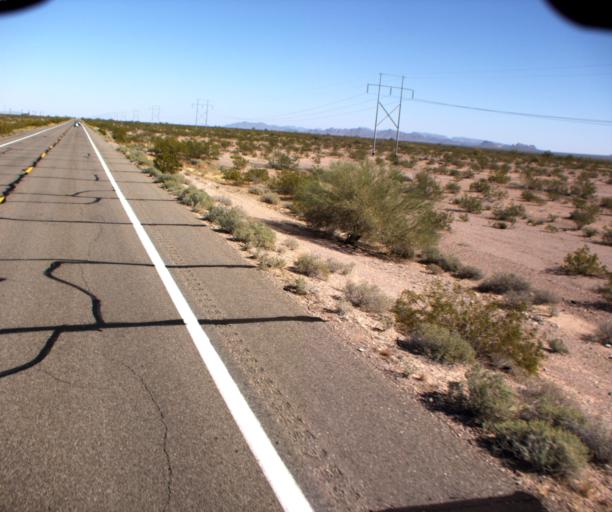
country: US
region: Arizona
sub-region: La Paz County
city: Quartzsite
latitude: 33.3298
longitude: -114.2169
